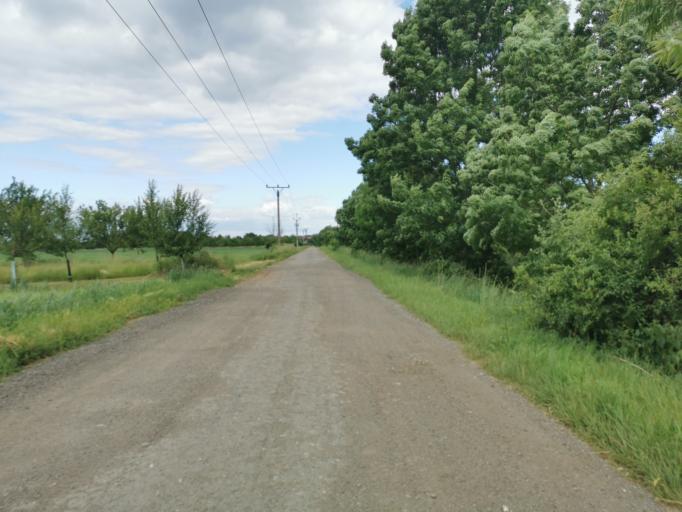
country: CZ
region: South Moravian
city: Vnorovy
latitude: 48.9295
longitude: 17.3338
